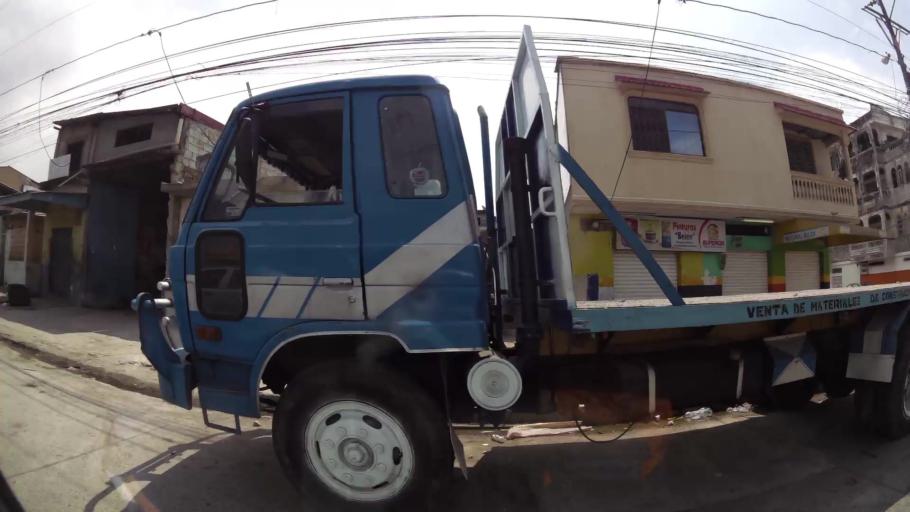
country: EC
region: Guayas
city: Guayaquil
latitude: -2.2591
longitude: -79.8866
